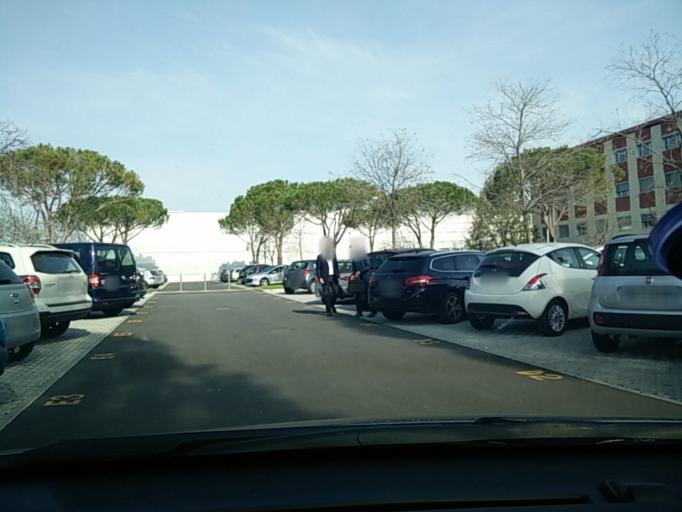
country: IT
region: Friuli Venezia Giulia
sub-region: Provincia di Udine
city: Buttrio
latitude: 46.0050
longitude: 13.3385
